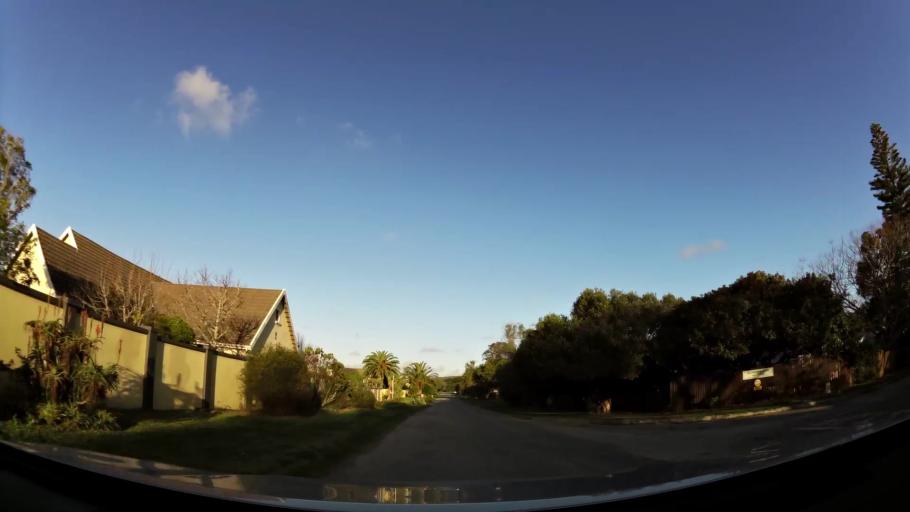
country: ZA
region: Western Cape
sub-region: Eden District Municipality
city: Knysna
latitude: -34.0130
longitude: 22.7805
